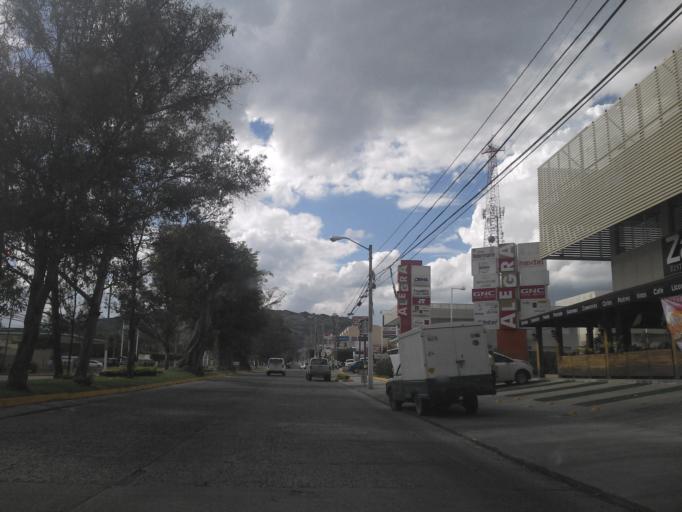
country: MX
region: Jalisco
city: Guadalajara
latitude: 20.6587
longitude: -103.4360
